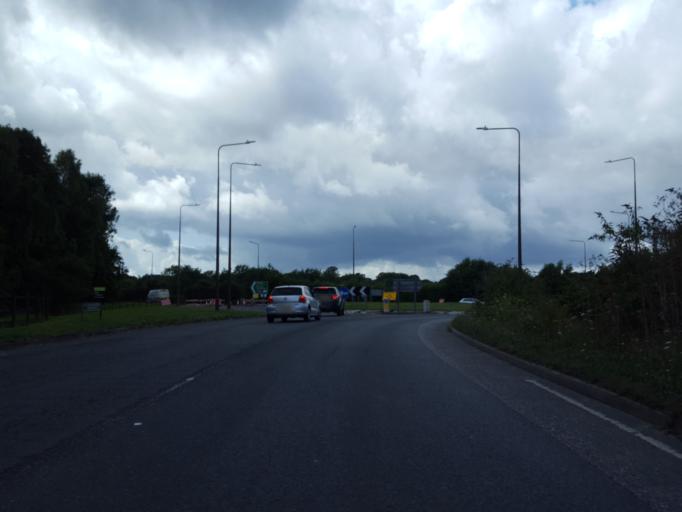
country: GB
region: England
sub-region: Kent
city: Kings Hill
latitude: 51.2798
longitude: 0.3957
